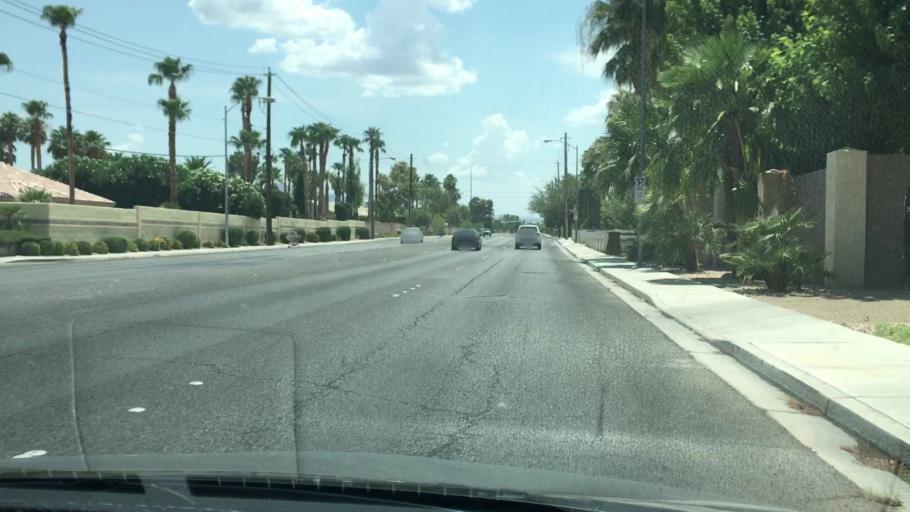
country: US
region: Nevada
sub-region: Clark County
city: Whitney
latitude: 36.0832
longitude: -115.0915
